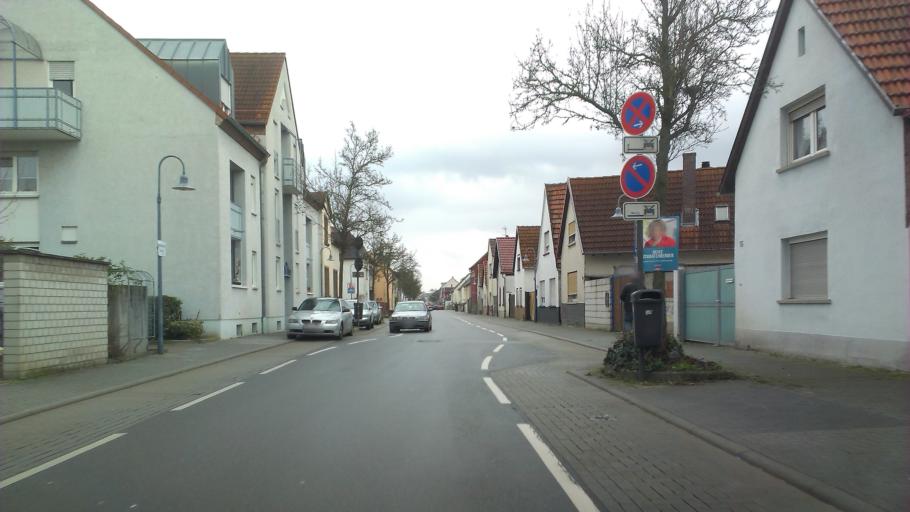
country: DE
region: Rheinland-Pfalz
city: Frankenthal
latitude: 49.4964
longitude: 8.3694
